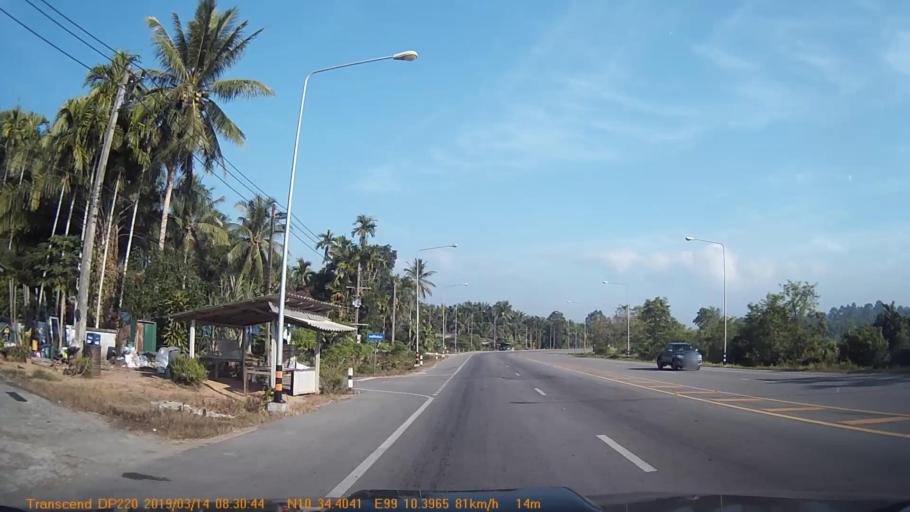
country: TH
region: Chumphon
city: Chumphon
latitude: 10.5736
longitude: 99.1731
